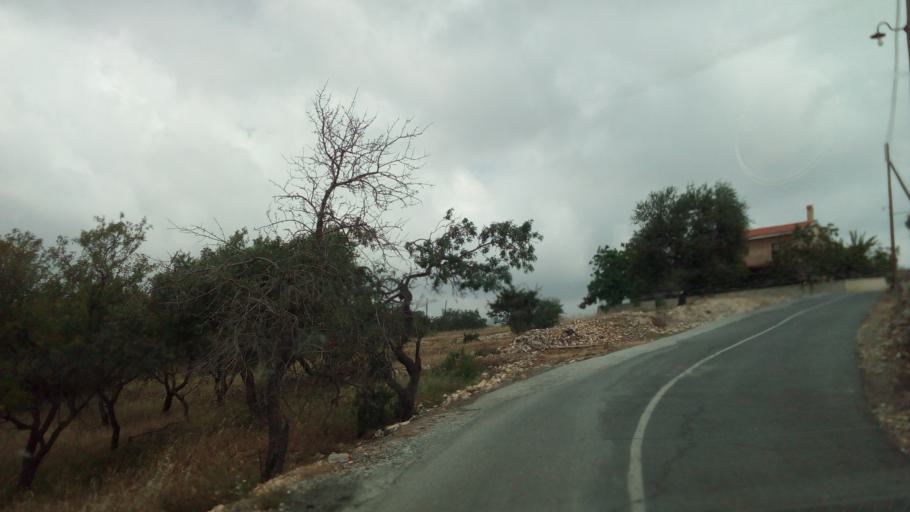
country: CY
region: Limassol
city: Pachna
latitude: 34.8149
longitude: 32.8705
